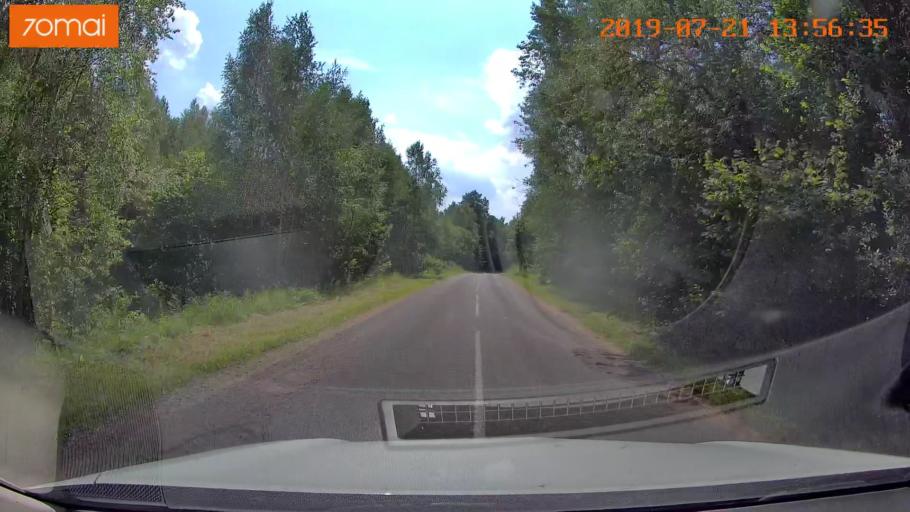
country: BY
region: Grodnenskaya
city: Lyubcha
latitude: 53.7782
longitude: 26.0990
